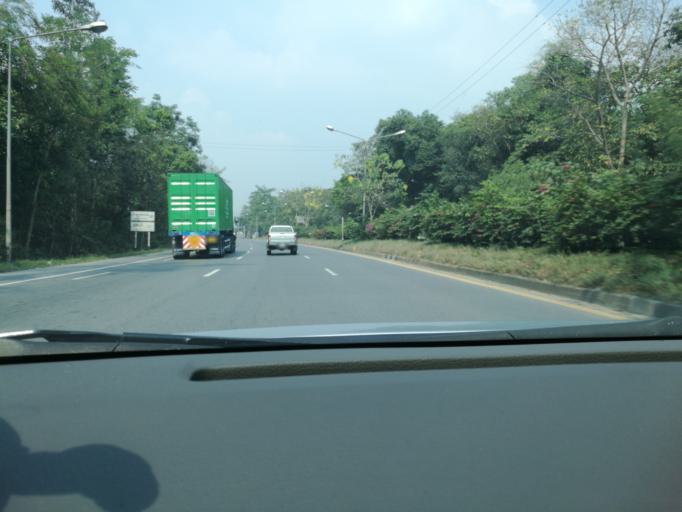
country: TH
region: Sara Buri
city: Chaloem Phra Kiat
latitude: 14.6688
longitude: 100.8872
